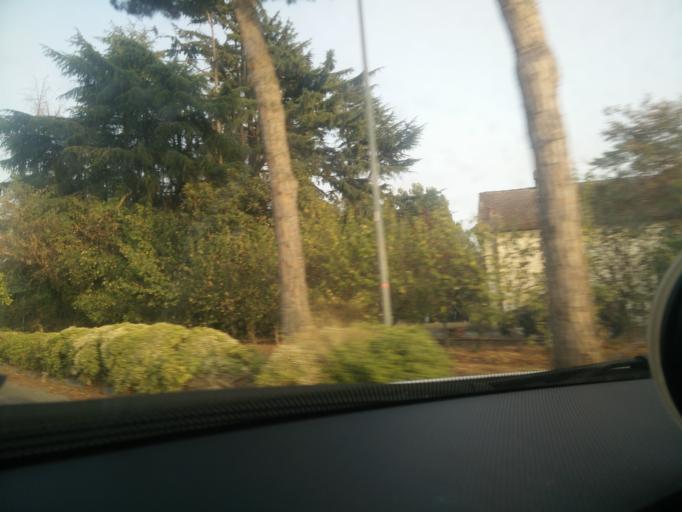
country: IT
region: Tuscany
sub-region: Provincia di Massa-Carrara
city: Massa
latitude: 44.0371
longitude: 10.1050
